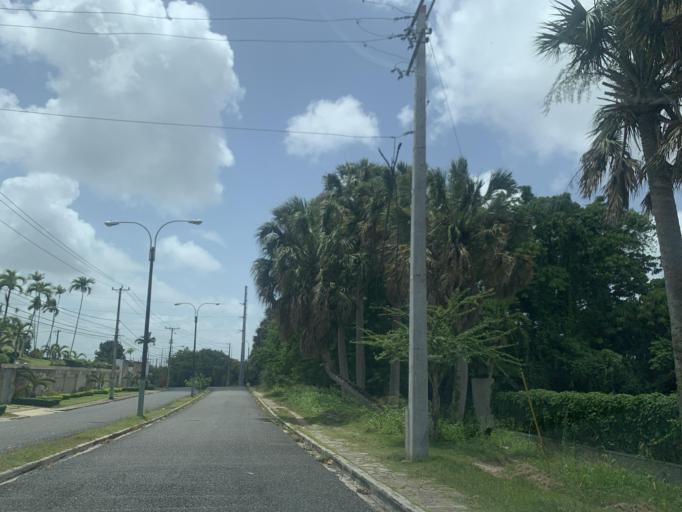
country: DO
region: Nacional
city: La Agustina
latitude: 18.5003
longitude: -69.9498
